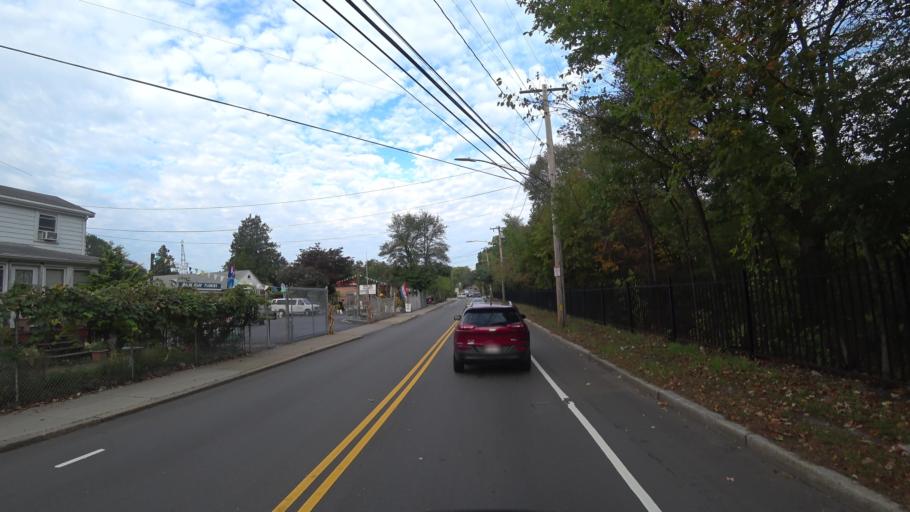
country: US
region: Massachusetts
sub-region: Suffolk County
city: Jamaica Plain
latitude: 42.2868
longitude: -71.1055
